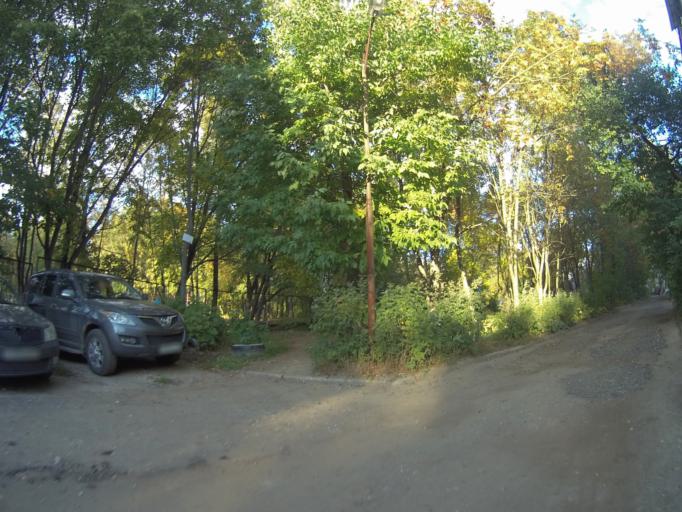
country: RU
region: Vladimir
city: Vladimir
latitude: 56.1136
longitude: 40.3481
